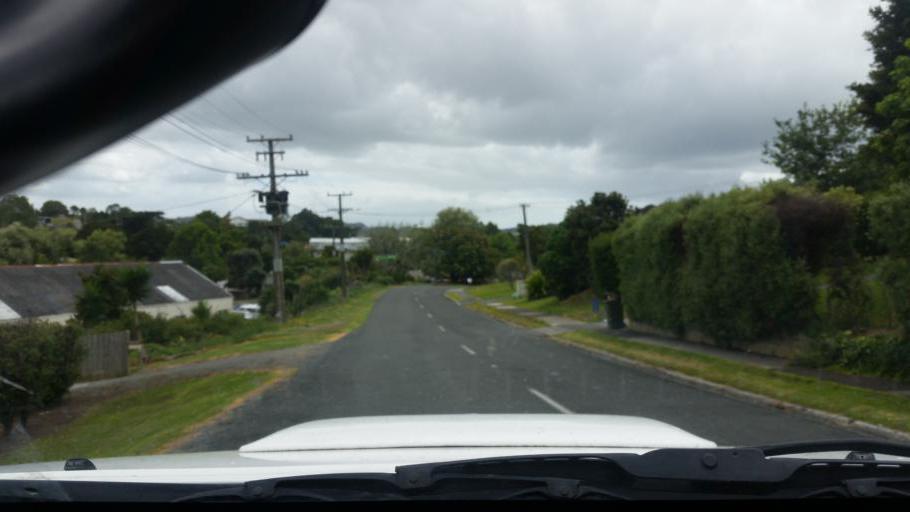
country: NZ
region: Northland
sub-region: Whangarei
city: Ruakaka
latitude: -36.1135
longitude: 174.3506
